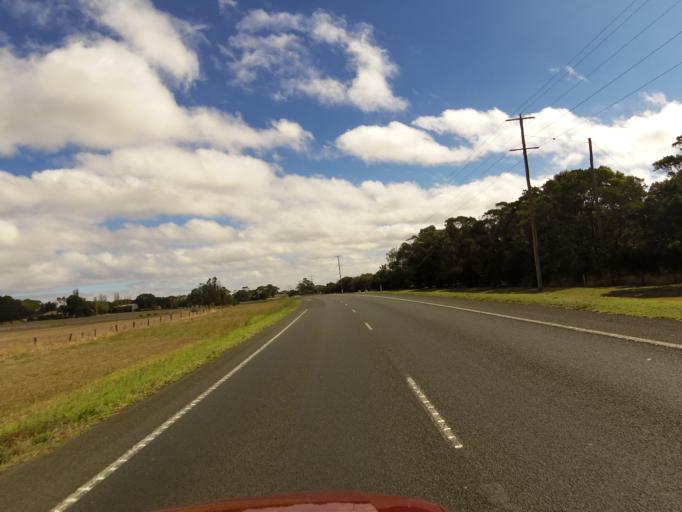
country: AU
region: Victoria
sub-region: Warrnambool
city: Allansford
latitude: -38.3369
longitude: 142.7118
